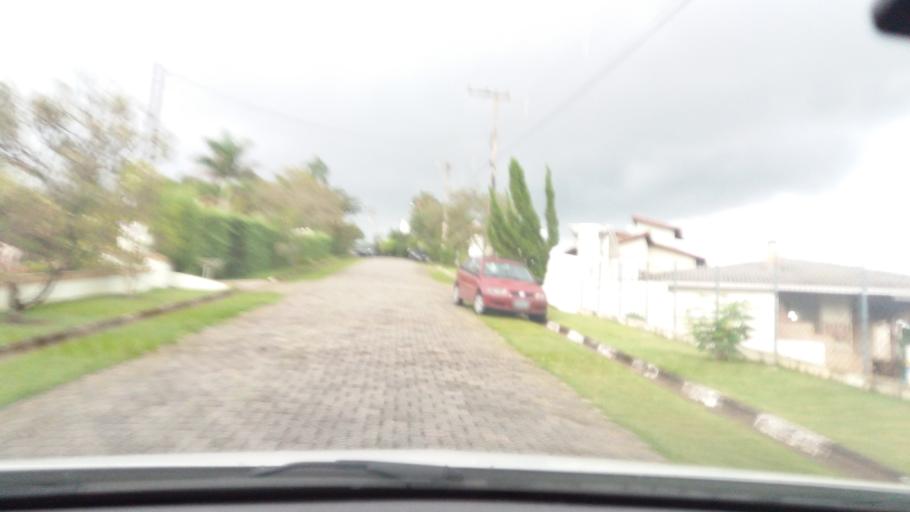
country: BR
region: Sao Paulo
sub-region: Bom Jesus Dos Perdoes
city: Bom Jesus dos Perdoes
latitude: -23.1687
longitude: -46.4639
